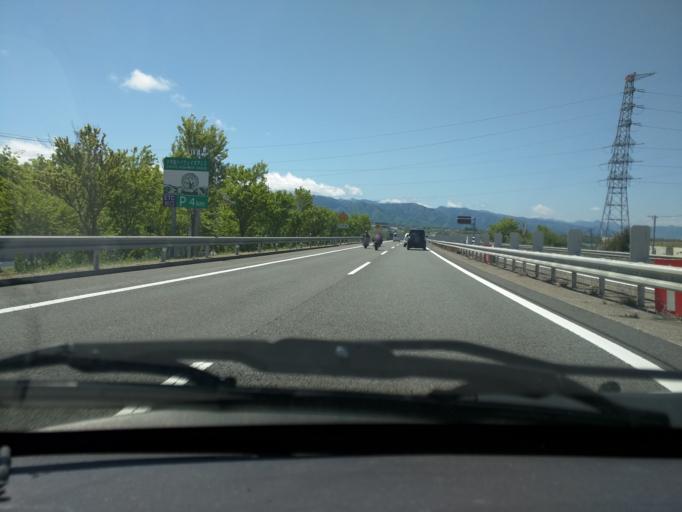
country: JP
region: Nagano
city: Nakano
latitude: 36.7269
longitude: 138.3165
